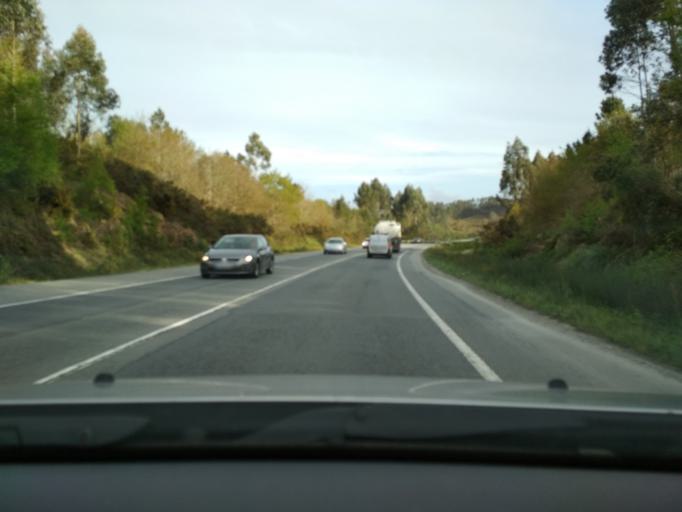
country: ES
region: Galicia
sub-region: Provincia da Coruna
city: Cerceda
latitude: 43.2232
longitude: -8.4590
